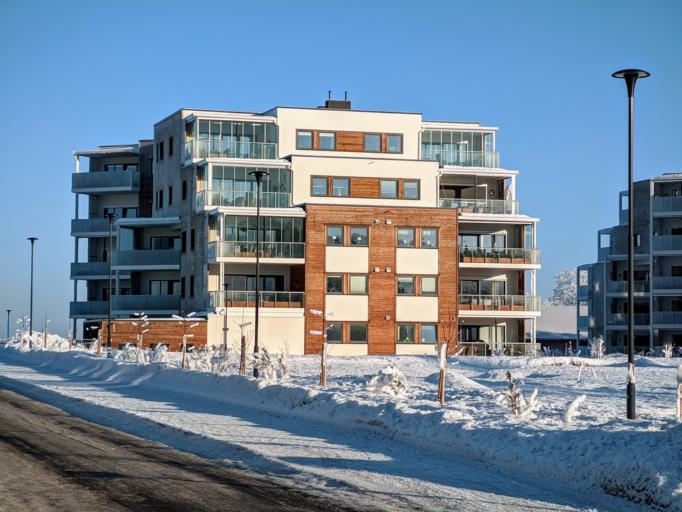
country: NO
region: Akershus
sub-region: Gjerdrum
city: Ask
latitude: 60.0697
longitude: 11.0371
